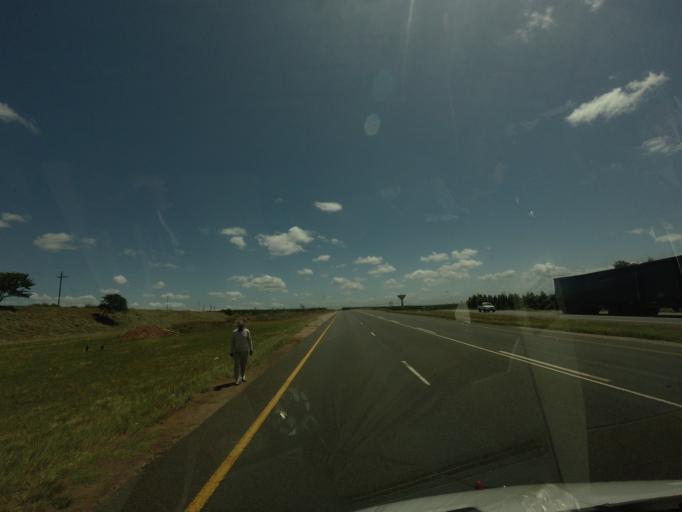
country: ZA
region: KwaZulu-Natal
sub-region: uThungulu District Municipality
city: Empangeni
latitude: -28.7721
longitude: 31.9297
